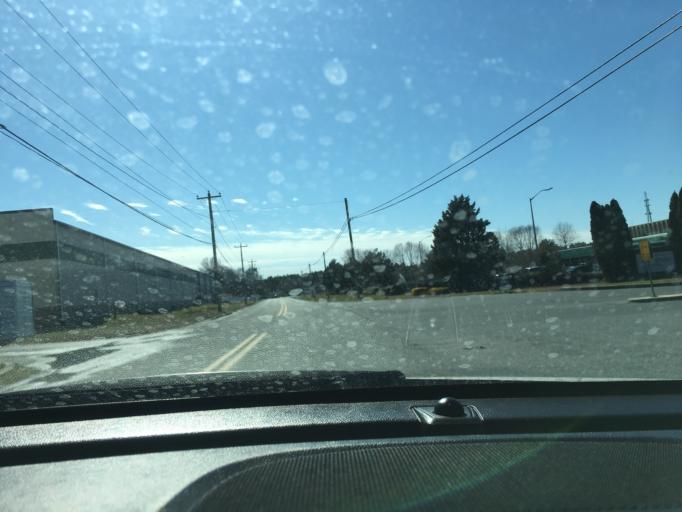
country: US
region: Maryland
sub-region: Wicomico County
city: Delmar
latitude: 38.4046
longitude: -75.5709
